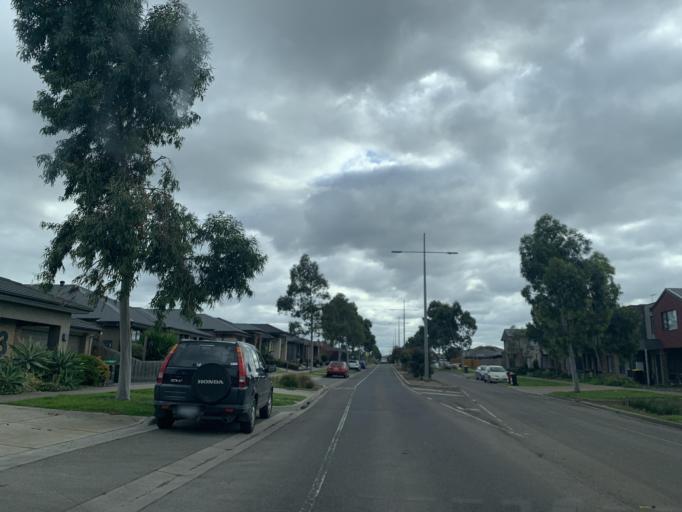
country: AU
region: Victoria
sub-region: Whittlesea
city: Epping
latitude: -37.6181
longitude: 145.0029
